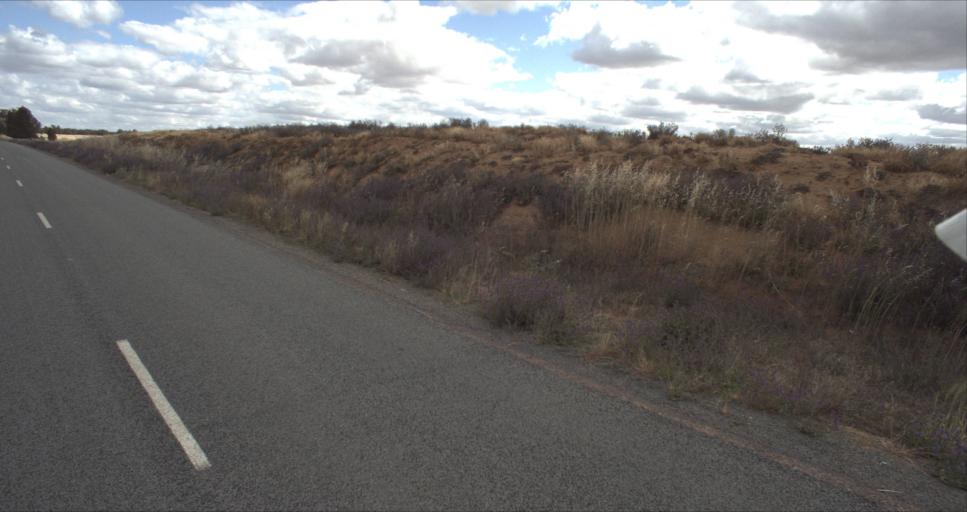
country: AU
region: New South Wales
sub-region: Leeton
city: Leeton
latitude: -34.6732
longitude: 146.3470
